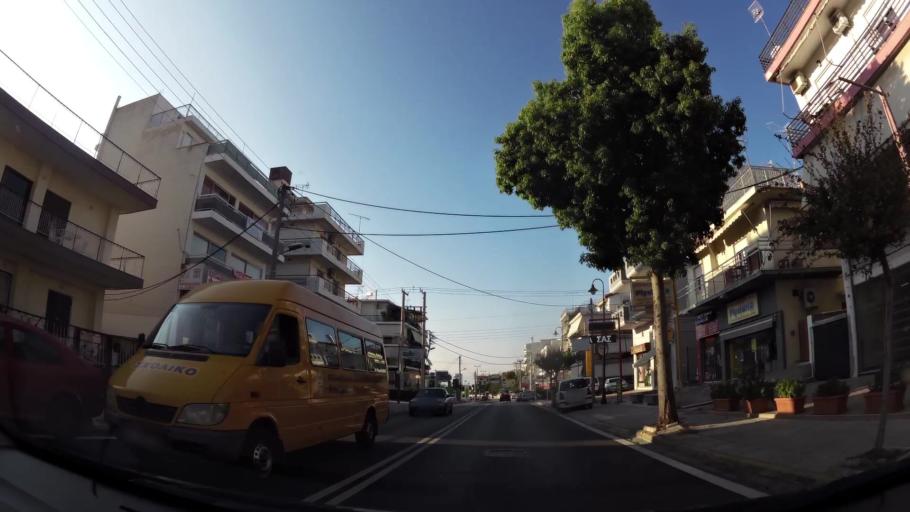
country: GR
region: Attica
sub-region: Nomarchia Athinas
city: Argyroupoli
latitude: 37.8948
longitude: 23.7622
